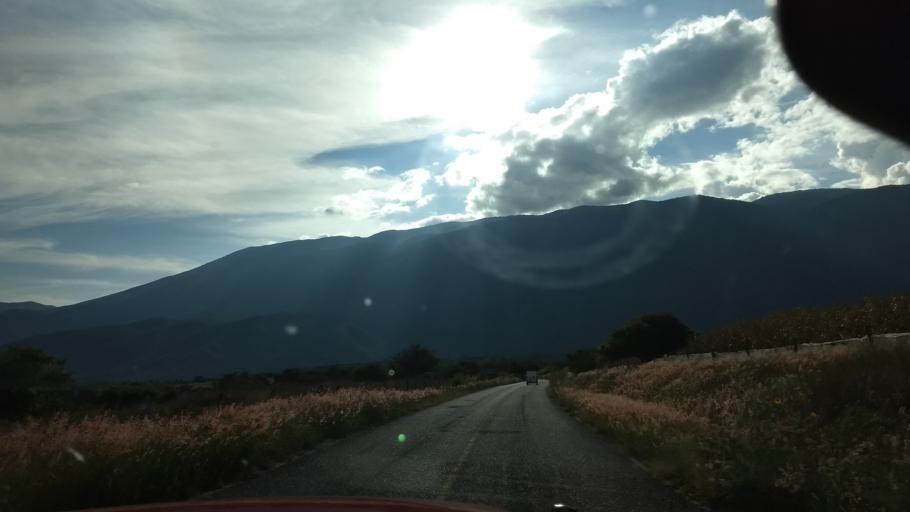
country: MX
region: Colima
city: Suchitlan
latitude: 19.4527
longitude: -103.8085
